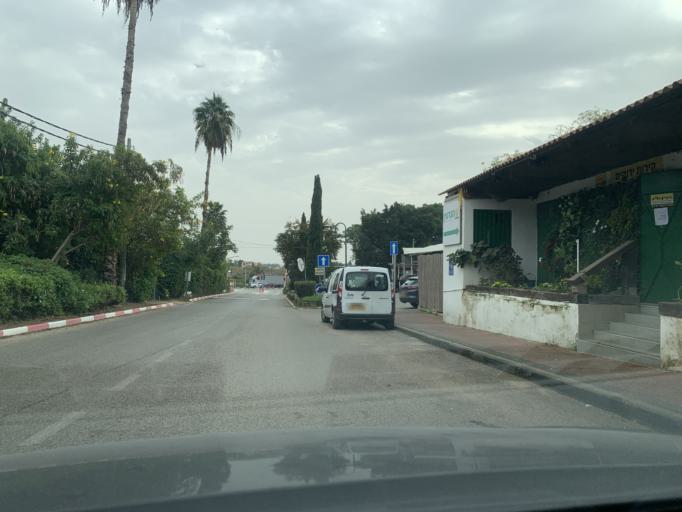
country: IL
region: Central District
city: Kfar Saba
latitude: 32.1938
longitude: 34.9083
